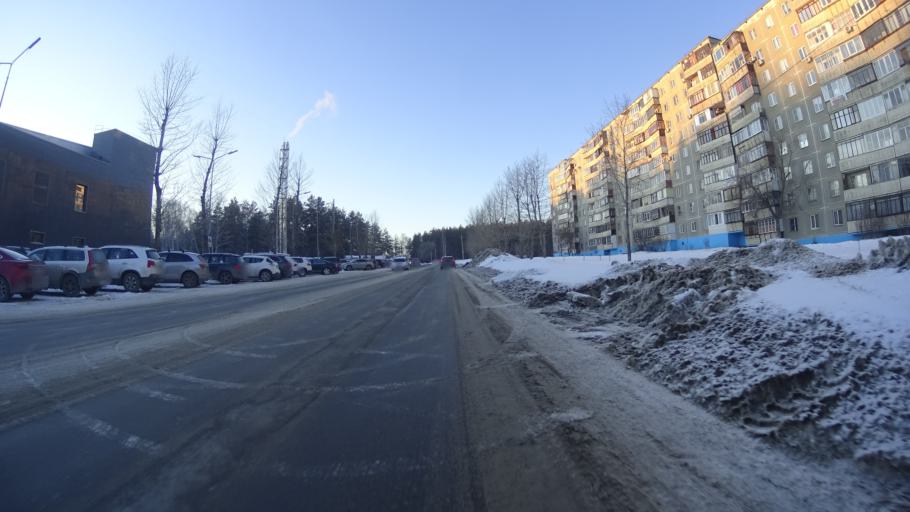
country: RU
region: Chelyabinsk
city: Roshchino
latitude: 55.1955
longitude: 61.2993
